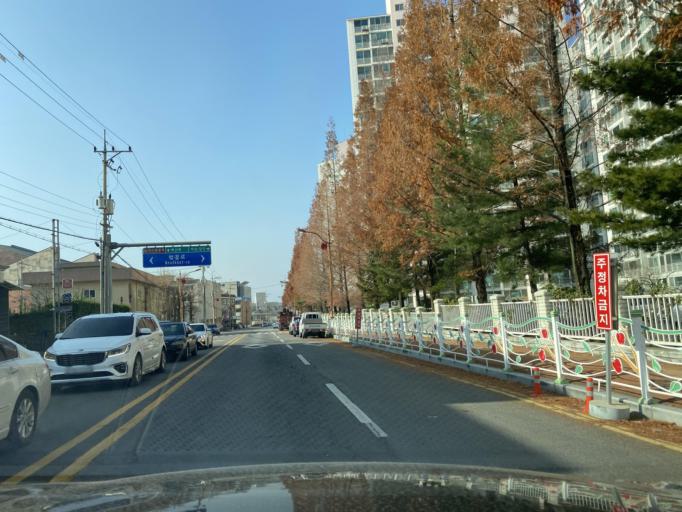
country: KR
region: Chungcheongnam-do
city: Yesan
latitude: 36.6866
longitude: 126.8360
